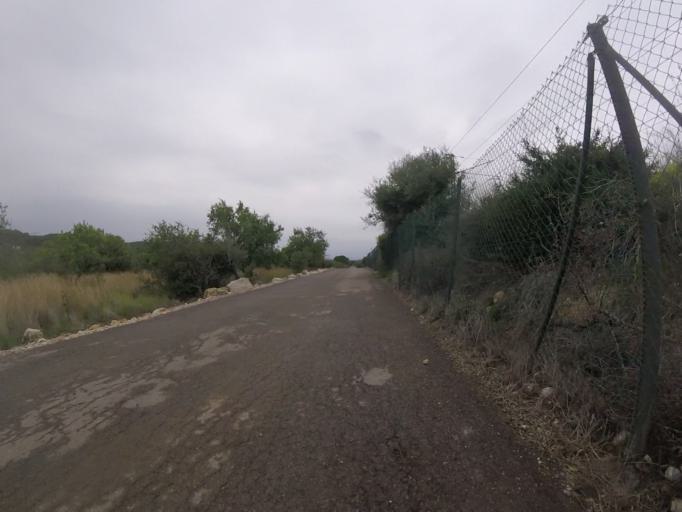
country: ES
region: Valencia
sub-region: Provincia de Castello
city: Alcala de Xivert
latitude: 40.2741
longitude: 0.2394
